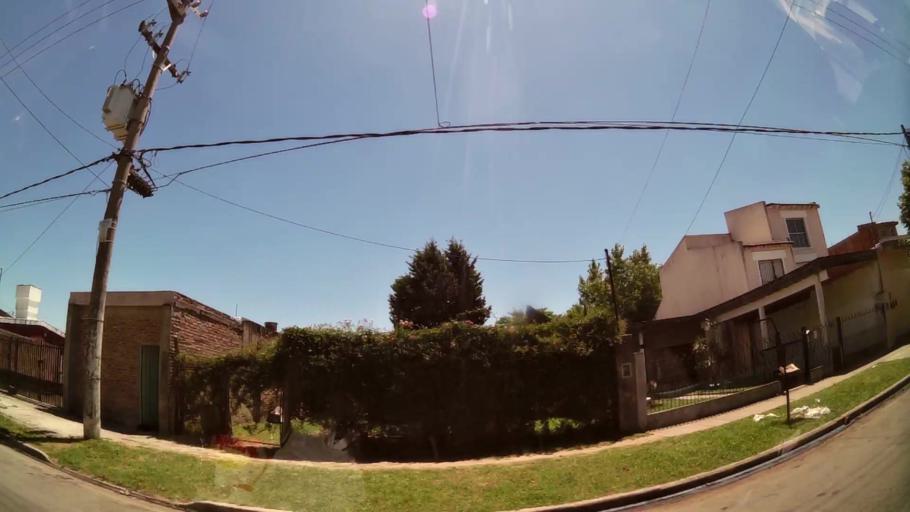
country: AR
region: Buenos Aires
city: Hurlingham
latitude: -34.5124
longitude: -58.7088
